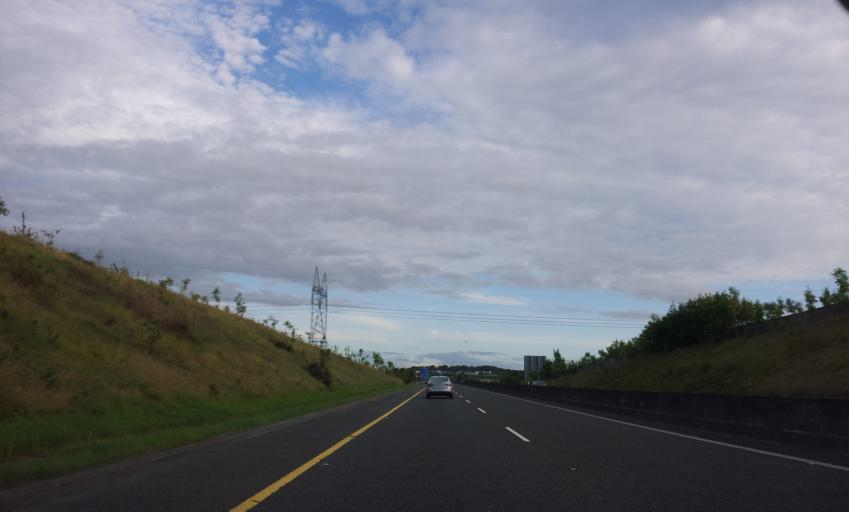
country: IE
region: Munster
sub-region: An Clar
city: Newmarket on Fergus
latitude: 52.8065
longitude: -8.9295
